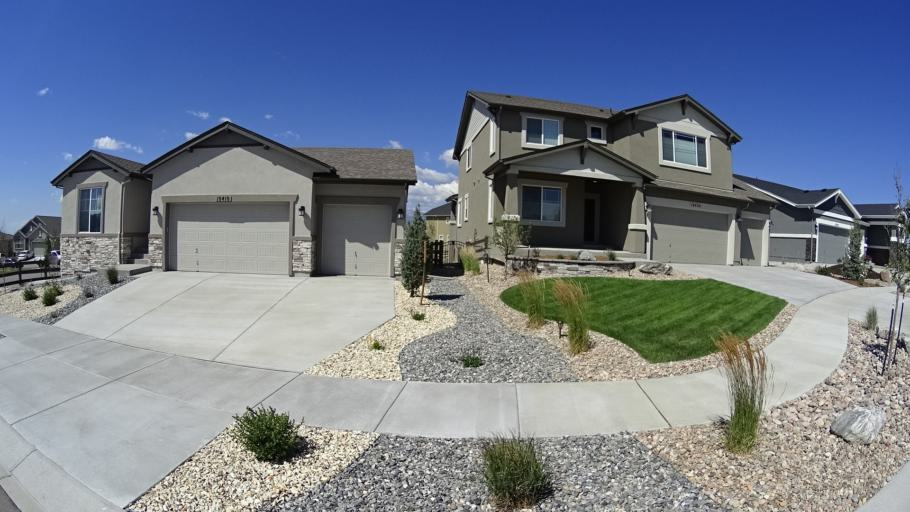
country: US
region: Colorado
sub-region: El Paso County
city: Black Forest
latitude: 38.9827
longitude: -104.7485
